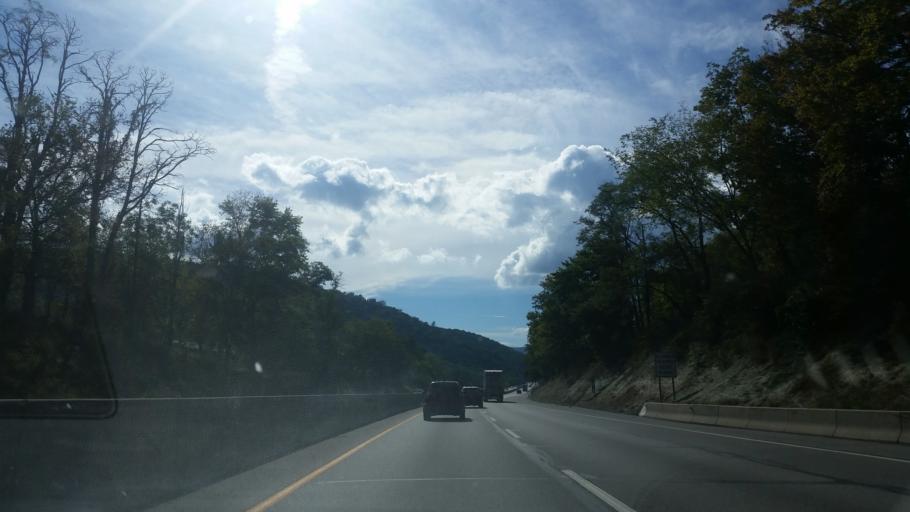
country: US
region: Pennsylvania
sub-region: Bedford County
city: Bedford
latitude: 40.0275
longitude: -78.4861
